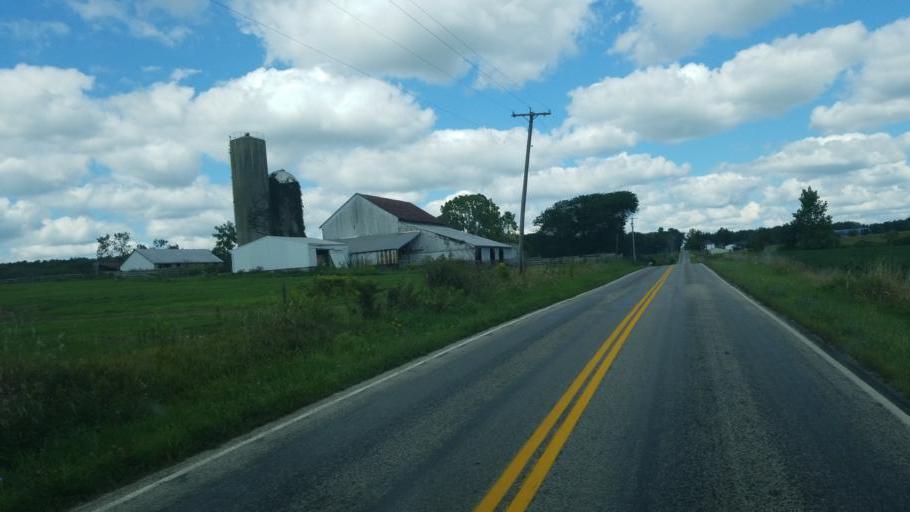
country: US
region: Ohio
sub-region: Ashland County
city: Ashland
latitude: 40.9602
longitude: -82.2820
